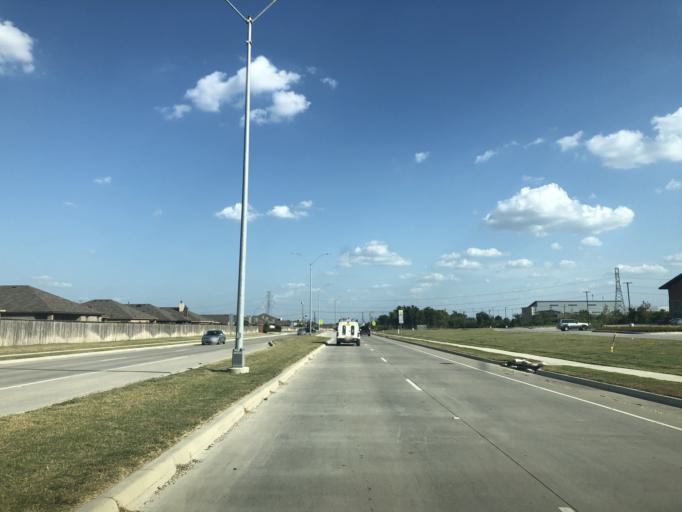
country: US
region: Texas
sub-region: Tarrant County
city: Saginaw
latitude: 32.8433
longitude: -97.3891
